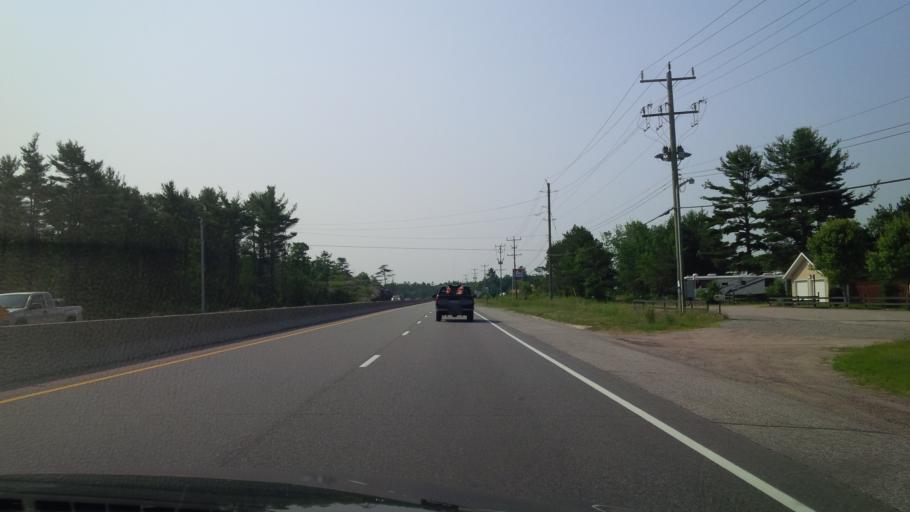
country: CA
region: Ontario
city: Gravenhurst
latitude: 44.8693
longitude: -79.3261
